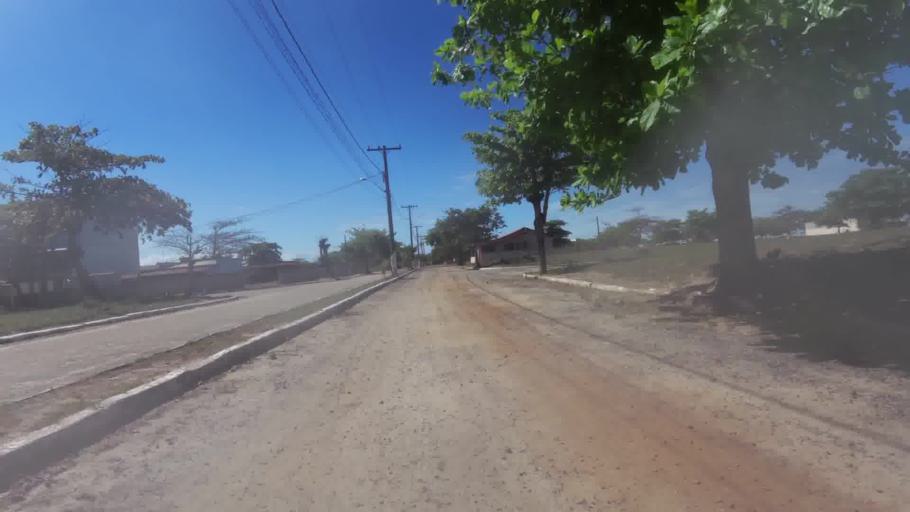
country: BR
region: Espirito Santo
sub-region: Marataizes
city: Marataizes
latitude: -21.1947
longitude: -40.9331
